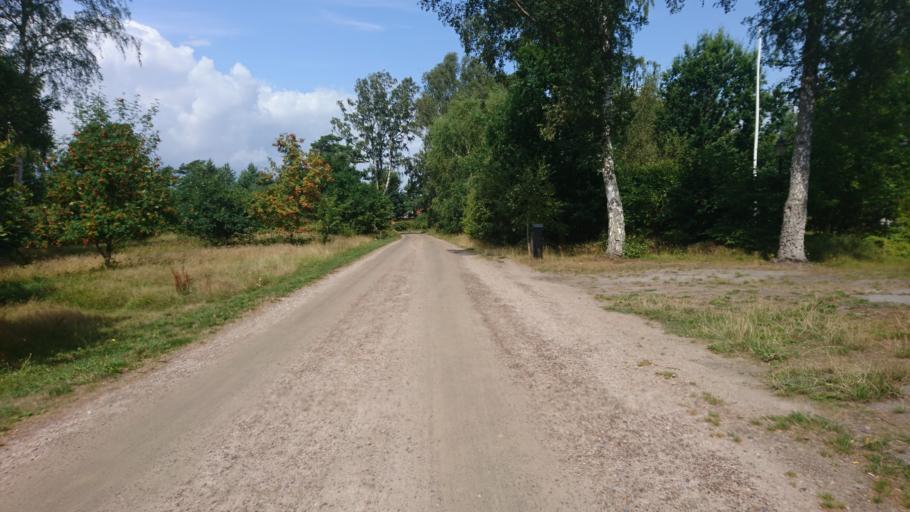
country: SE
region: Skane
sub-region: Vellinge Kommun
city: Ljunghusen
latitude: 55.3920
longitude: 12.9115
